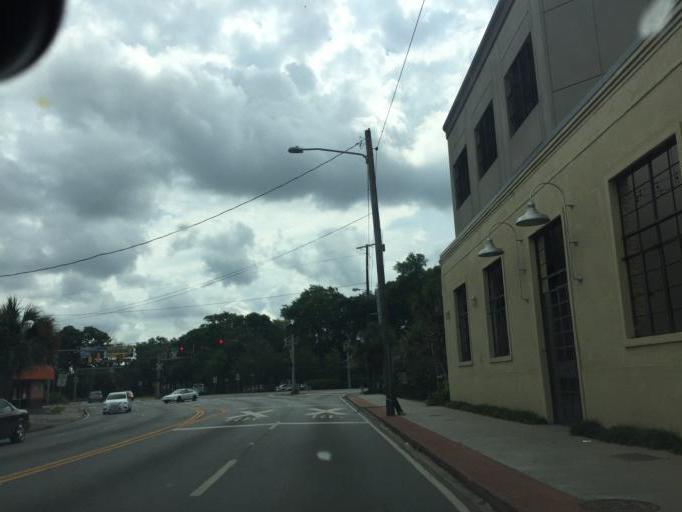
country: US
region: Georgia
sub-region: Chatham County
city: Savannah
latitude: 32.0525
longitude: -81.1029
